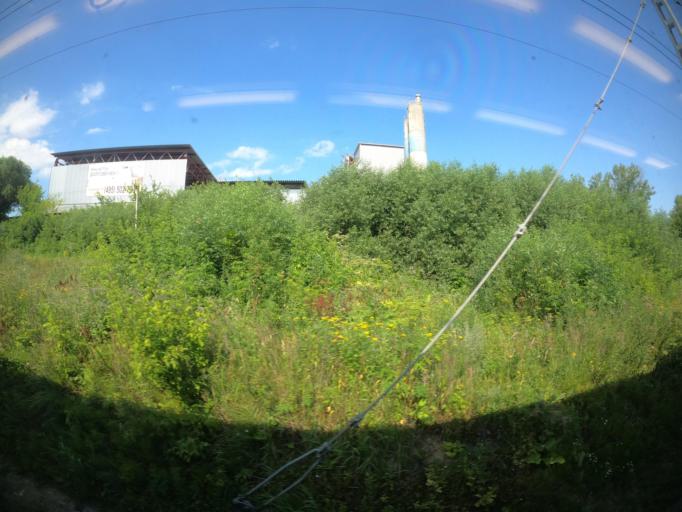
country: RU
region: Moskovskaya
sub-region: Podol'skiy Rayon
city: Podol'sk
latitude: 55.4135
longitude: 37.5552
